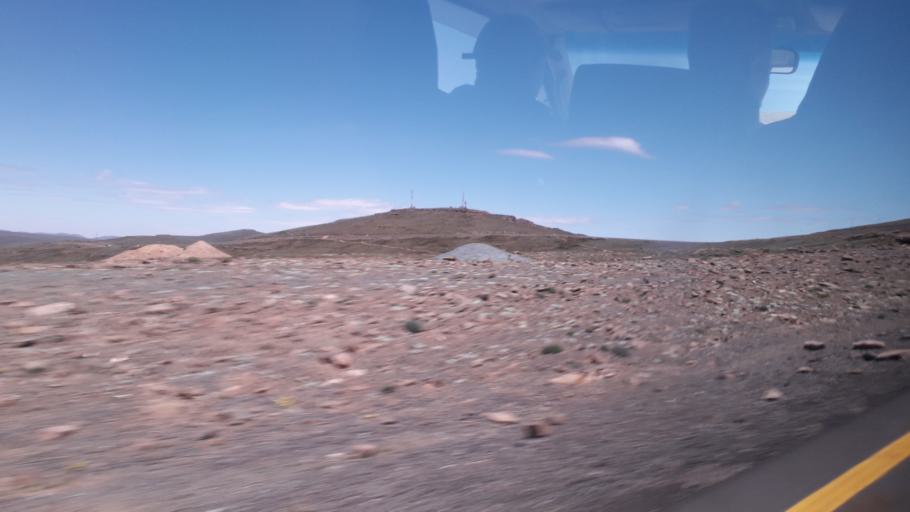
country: ZA
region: Orange Free State
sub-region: Thabo Mofutsanyana District Municipality
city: Phuthaditjhaba
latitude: -28.8112
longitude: 28.7333
